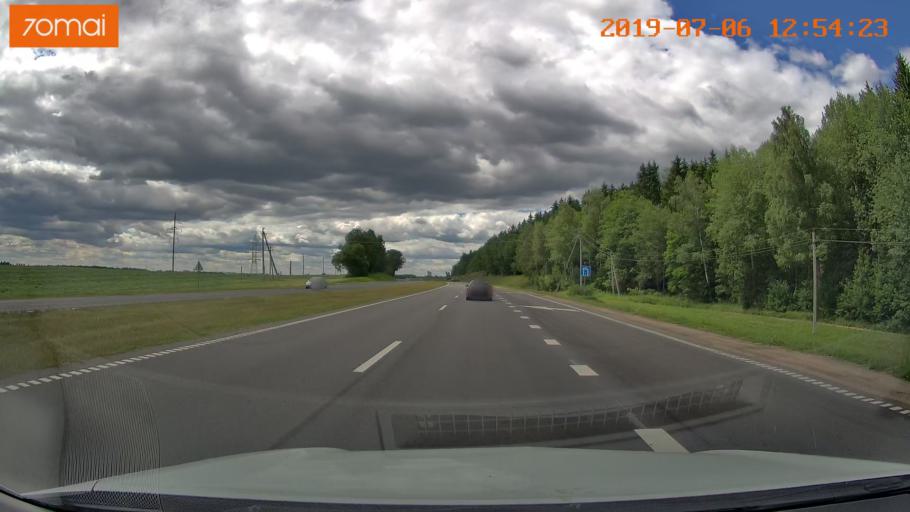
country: BY
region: Minsk
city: Dzyarzhynsk
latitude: 53.7019
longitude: 27.1898
